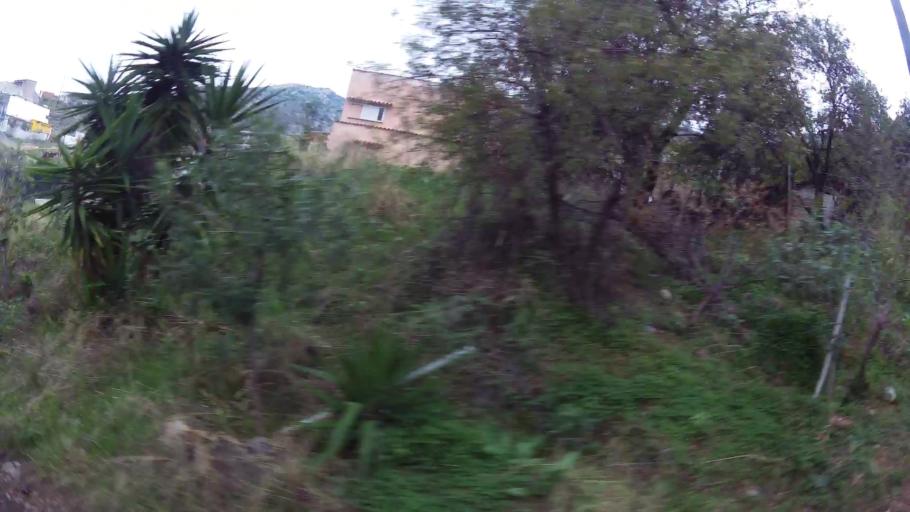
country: GR
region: Attica
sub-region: Nomos Piraios
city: Korydallos
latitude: 37.9955
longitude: 23.6399
